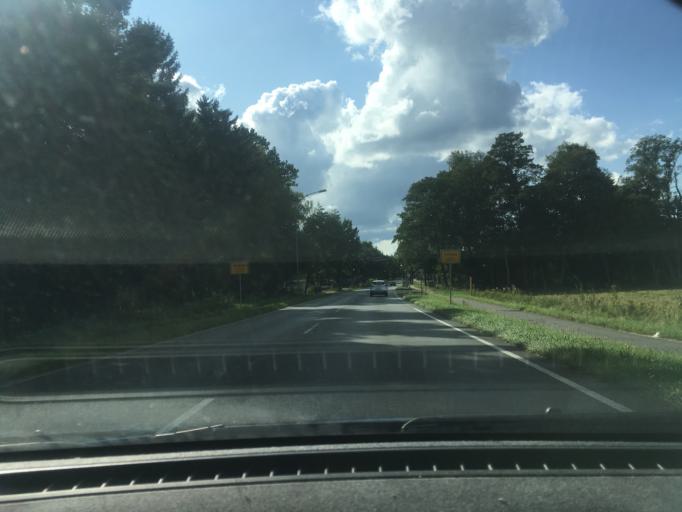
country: DE
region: Lower Saxony
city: Soltau
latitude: 52.9872
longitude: 9.8806
